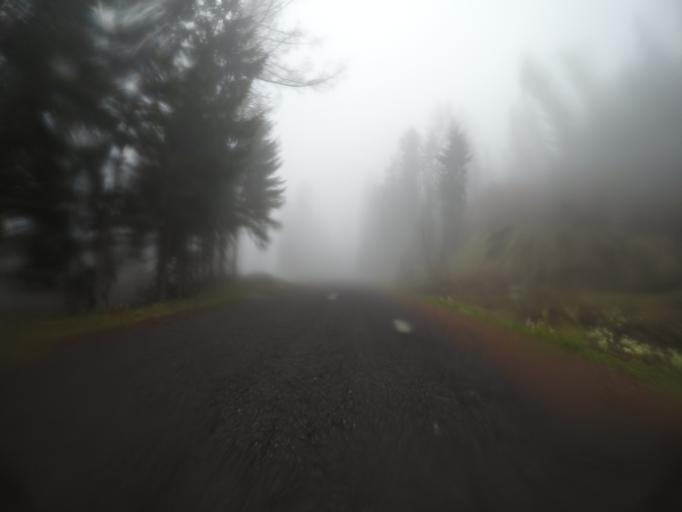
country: SK
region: Presovsky
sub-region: Okres Poprad
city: Strba
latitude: 49.1202
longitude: 20.0702
